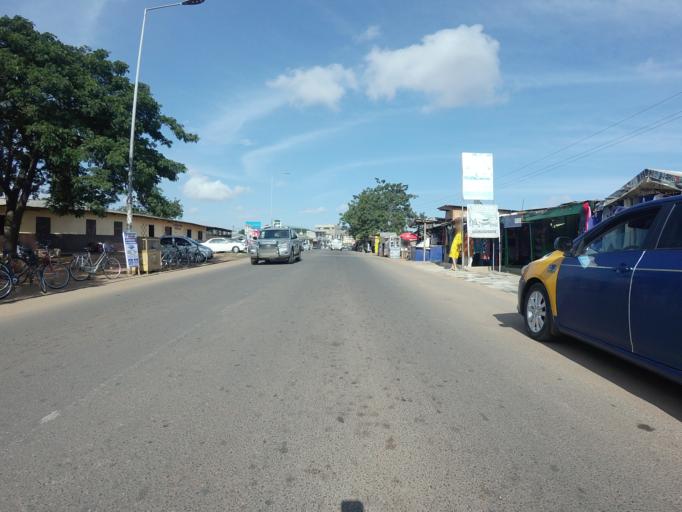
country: GH
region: Greater Accra
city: Medina Estates
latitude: 5.6418
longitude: -0.1678
